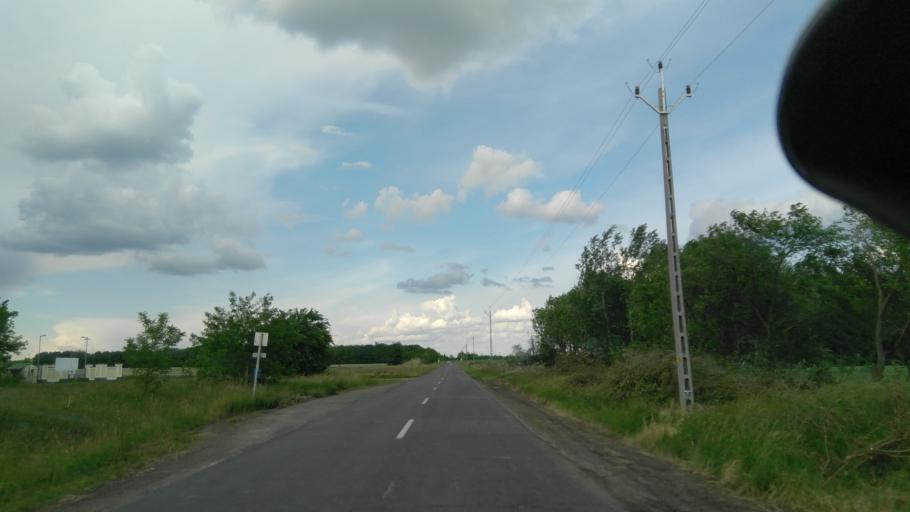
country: HU
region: Bekes
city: Dombegyhaz
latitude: 46.3315
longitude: 21.1031
